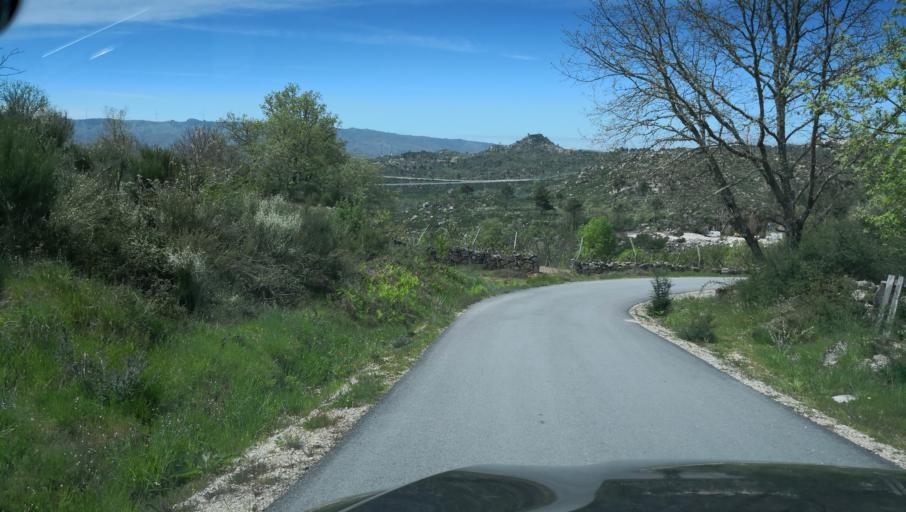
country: PT
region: Vila Real
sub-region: Vila Real
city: Vila Real
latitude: 41.3643
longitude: -7.6700
